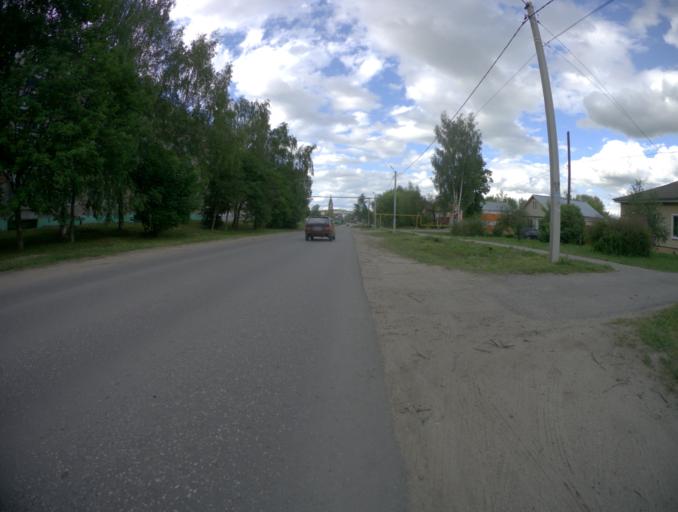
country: RU
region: Vladimir
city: Yur'yev-Pol'skiy
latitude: 56.4909
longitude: 39.6717
